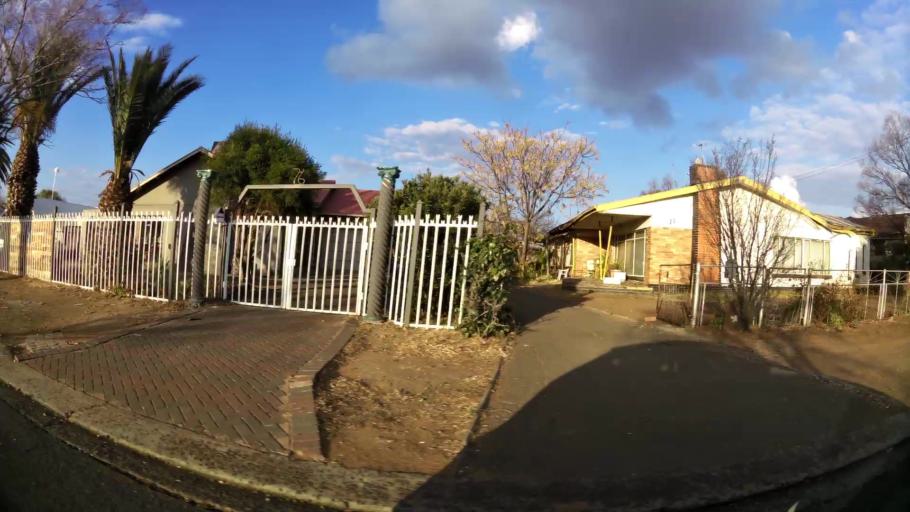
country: ZA
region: Orange Free State
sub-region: Mangaung Metropolitan Municipality
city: Bloemfontein
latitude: -29.1375
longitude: 26.1904
